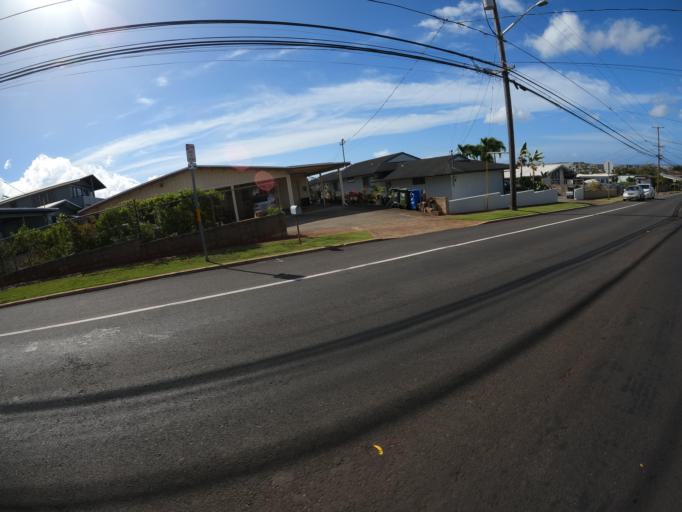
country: US
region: Hawaii
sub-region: Honolulu County
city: Halawa Heights
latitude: 21.3764
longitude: -157.9173
